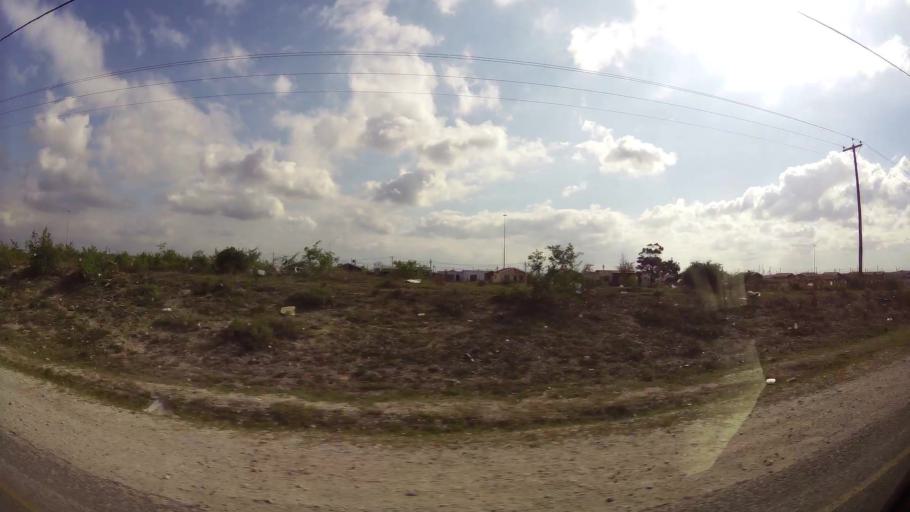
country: ZA
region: Eastern Cape
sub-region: Nelson Mandela Bay Metropolitan Municipality
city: Port Elizabeth
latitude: -33.7742
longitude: 25.5909
